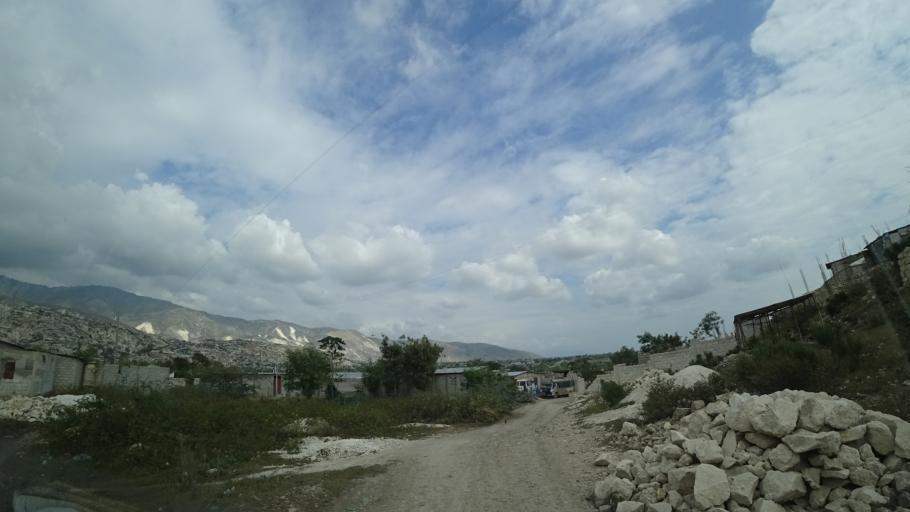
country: HT
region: Ouest
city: Croix des Bouquets
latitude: 18.6633
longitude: -72.2565
